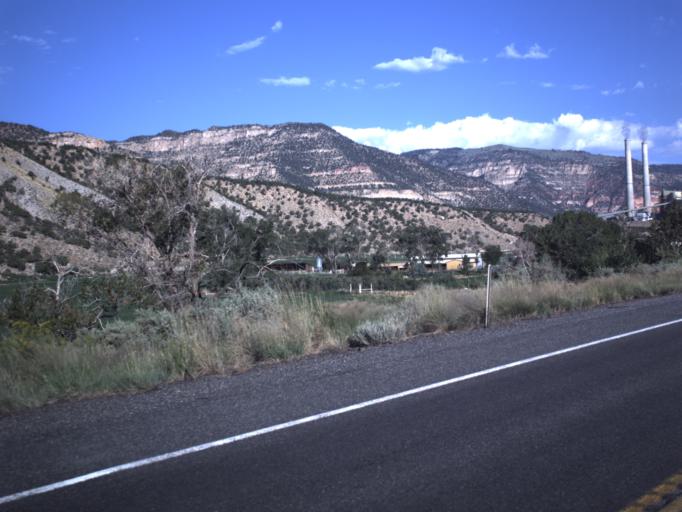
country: US
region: Utah
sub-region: Emery County
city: Huntington
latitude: 39.3697
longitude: -111.0597
